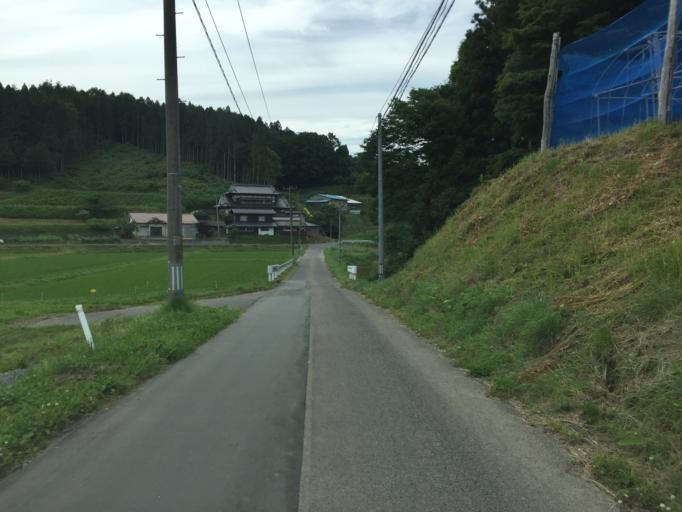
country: JP
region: Fukushima
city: Funehikimachi-funehiki
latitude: 37.5001
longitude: 140.6512
